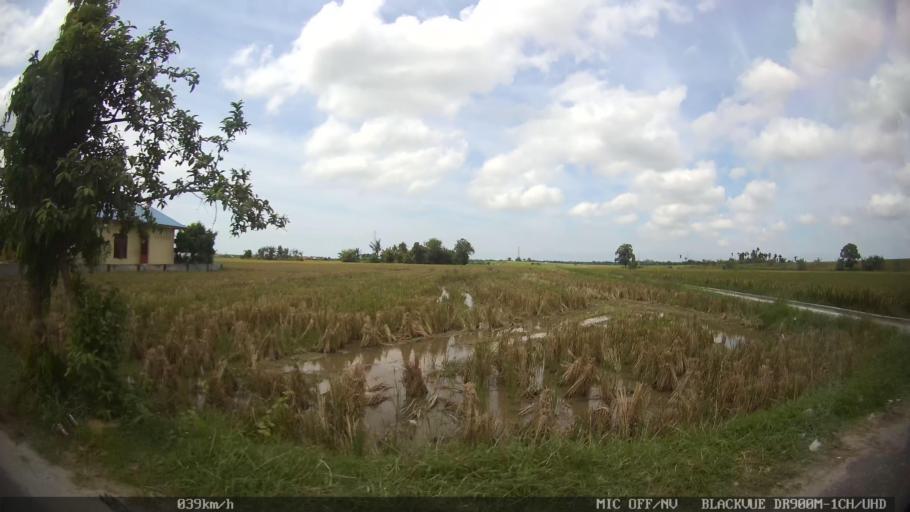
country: ID
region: North Sumatra
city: Percut
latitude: 3.5720
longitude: 98.8457
